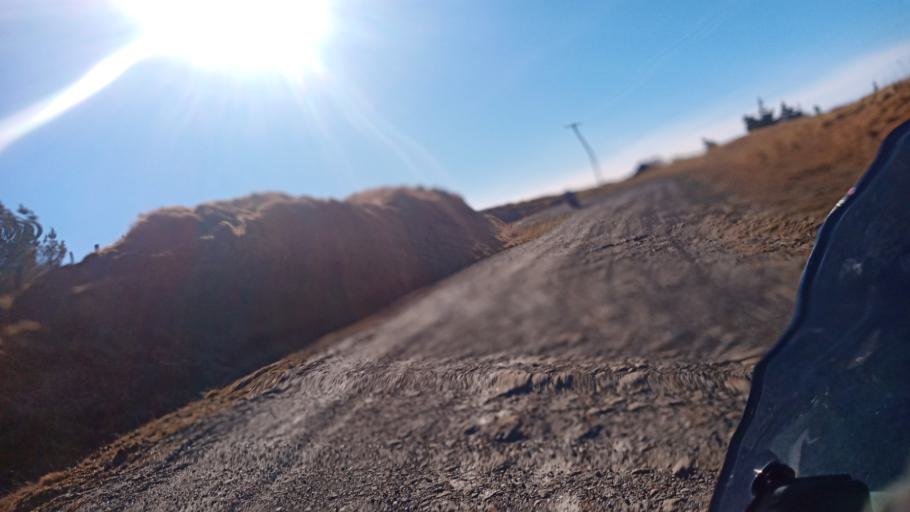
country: NZ
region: Gisborne
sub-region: Gisborne District
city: Gisborne
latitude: -38.1883
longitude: 177.8187
